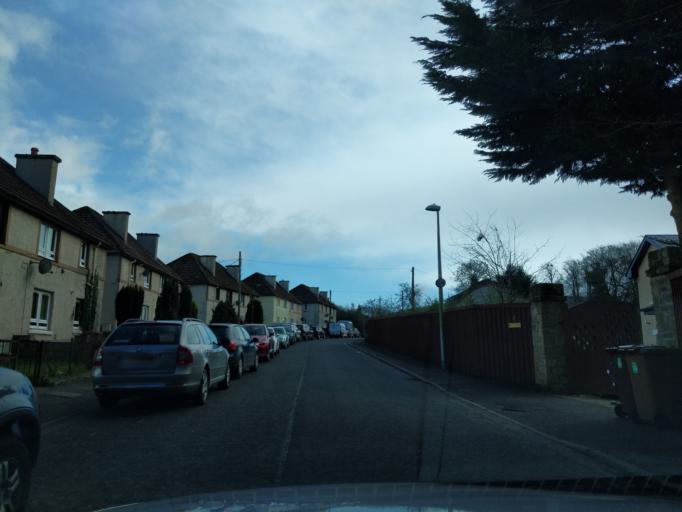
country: GB
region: Scotland
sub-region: Edinburgh
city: Balerno
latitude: 55.8787
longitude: -3.3324
